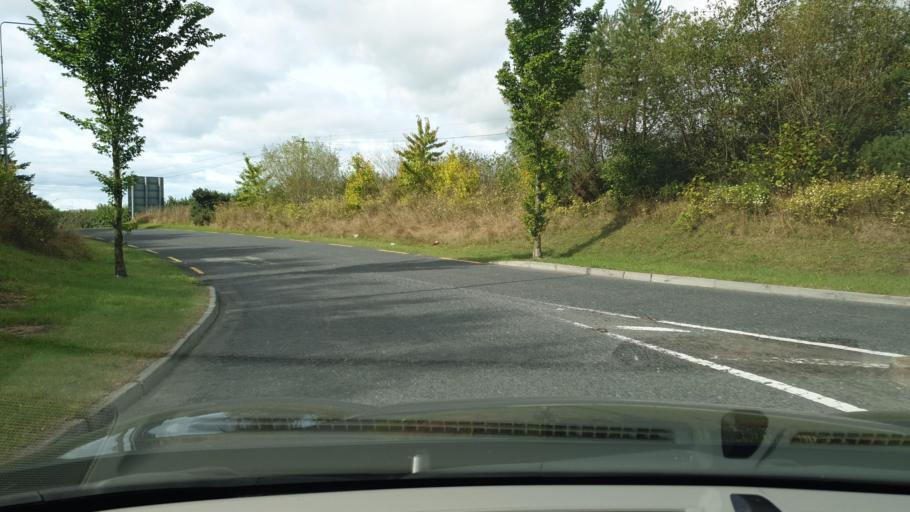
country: IE
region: Leinster
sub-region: Laois
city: Portlaoise
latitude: 53.0516
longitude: -7.2422
